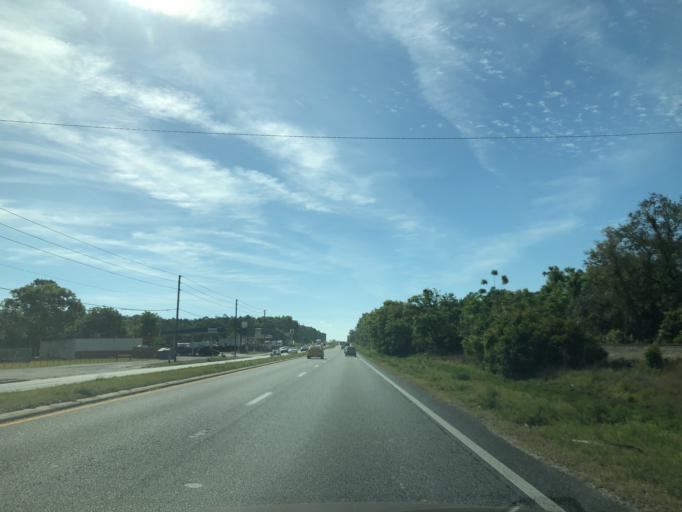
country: US
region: Florida
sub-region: Orange County
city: Zellwood
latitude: 28.7243
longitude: -81.5986
